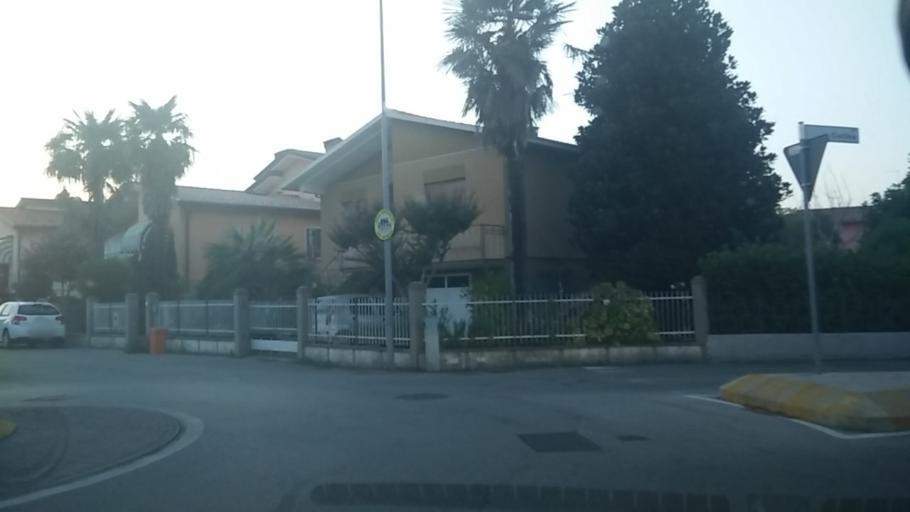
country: IT
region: Veneto
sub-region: Provincia di Venezia
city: San Dona di Piave
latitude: 45.6429
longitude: 12.5565
